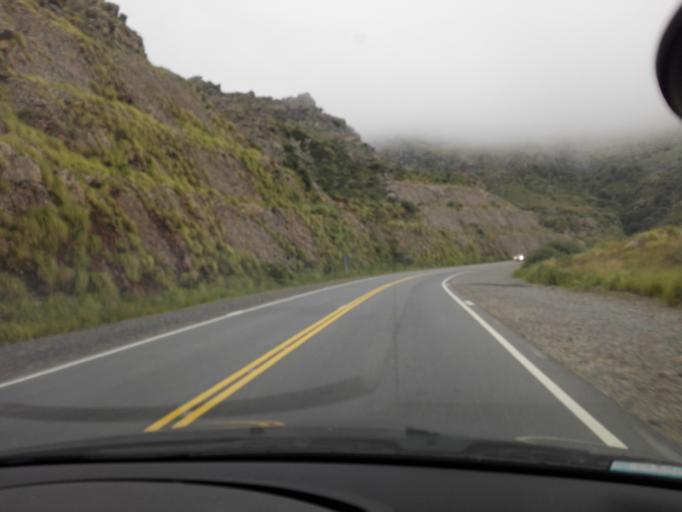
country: AR
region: Cordoba
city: Cuesta Blanca
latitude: -31.6152
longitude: -64.6899
